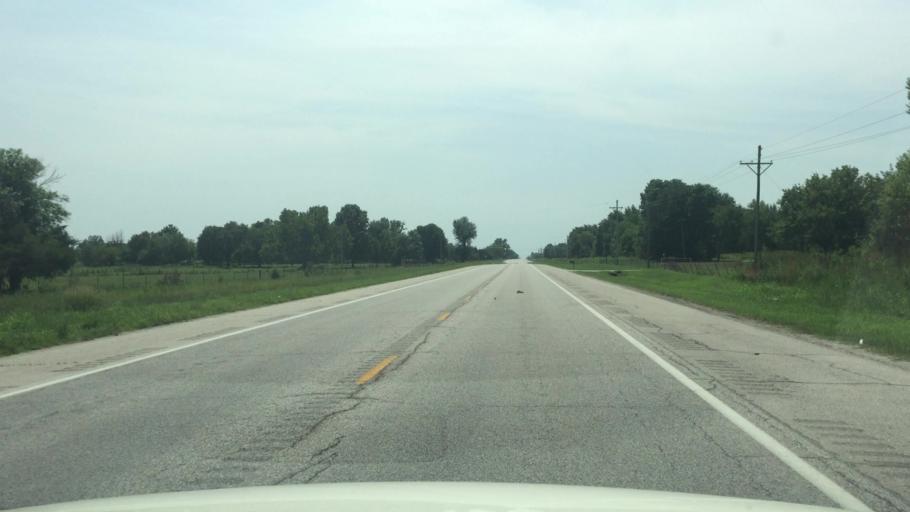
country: US
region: Kansas
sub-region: Cherokee County
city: Galena
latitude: 37.1261
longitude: -94.7044
